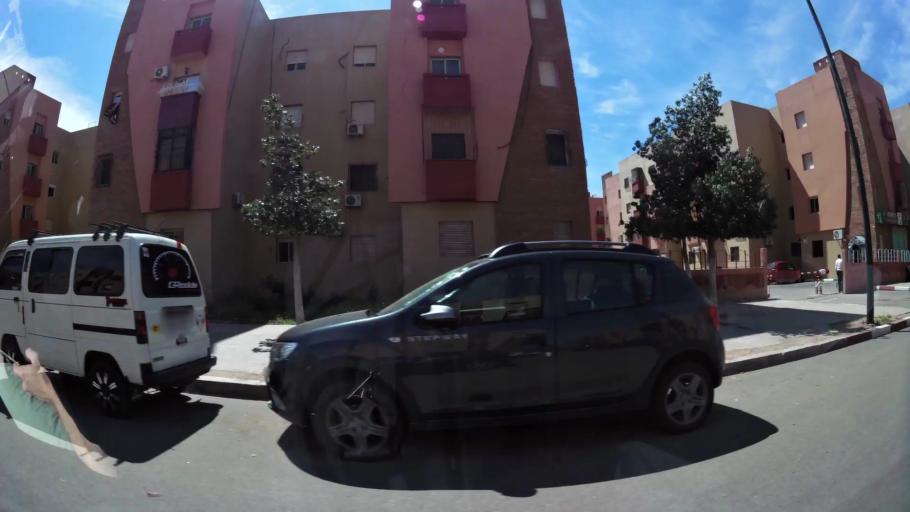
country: MA
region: Marrakech-Tensift-Al Haouz
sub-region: Marrakech
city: Marrakesh
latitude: 31.6377
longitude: -8.0782
